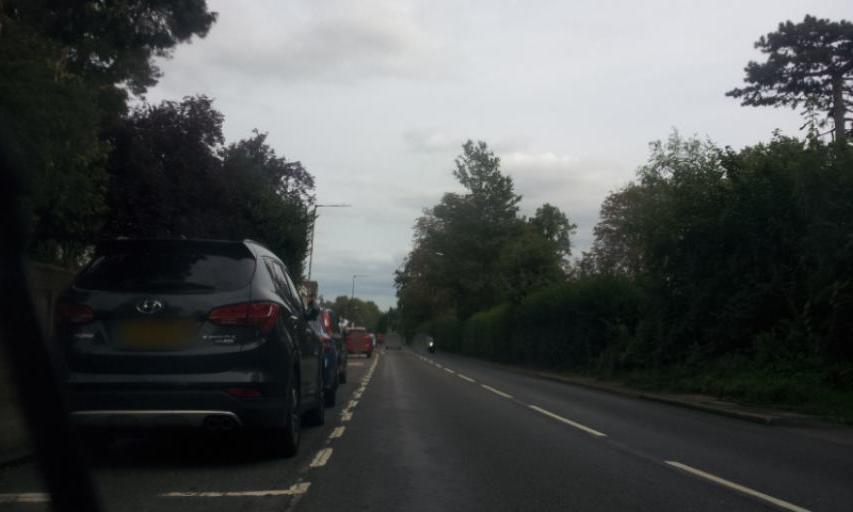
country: GB
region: England
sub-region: Kent
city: Tonbridge
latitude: 51.2162
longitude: 0.2417
